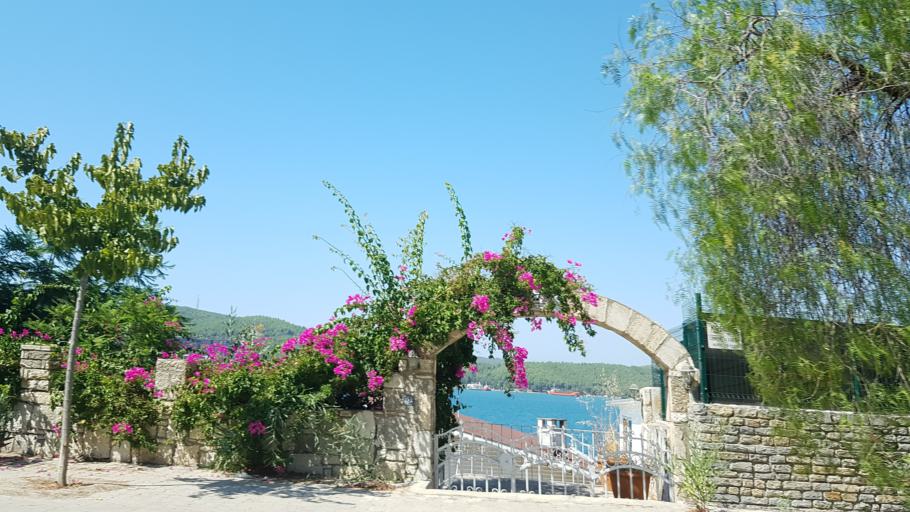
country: TR
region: Mugla
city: Karaova
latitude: 37.1272
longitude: 27.5726
